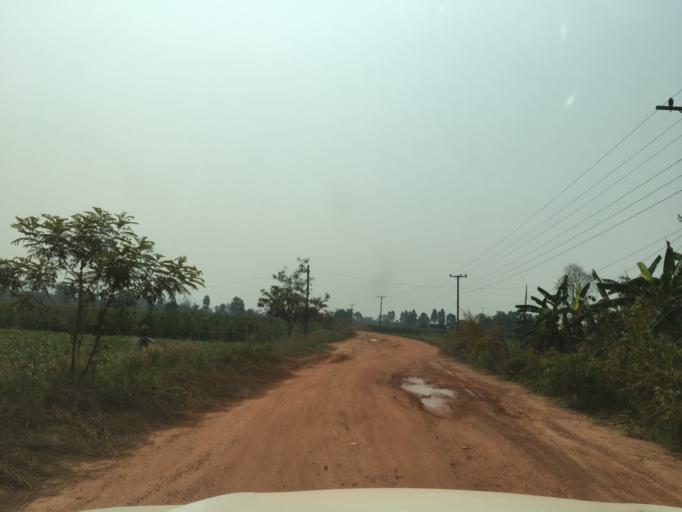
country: TH
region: Changwat Bueng Kan
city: Bung Khla
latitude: 18.2208
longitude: 104.0671
